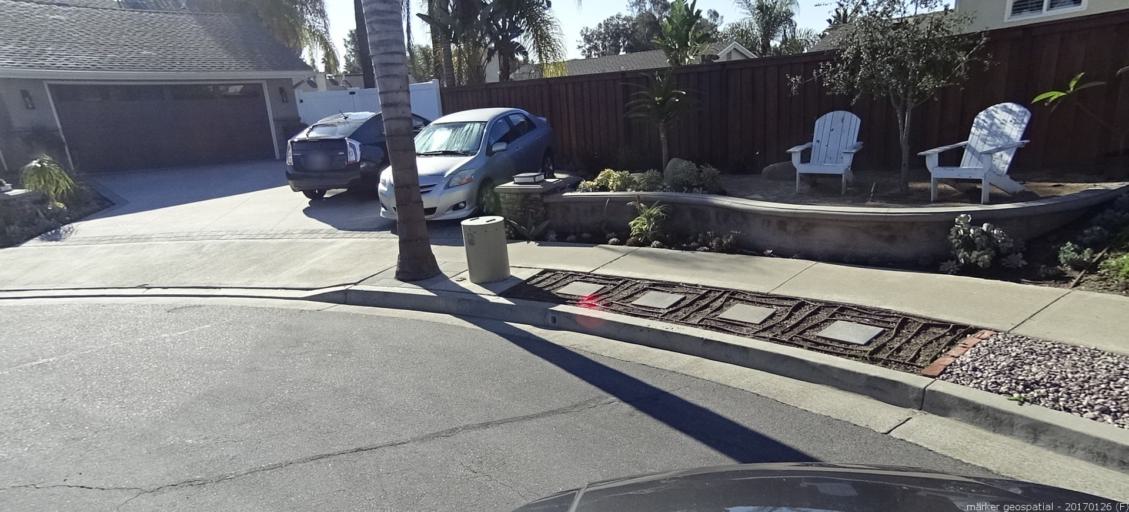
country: US
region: California
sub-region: Orange County
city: Lake Forest
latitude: 33.6340
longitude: -117.6817
